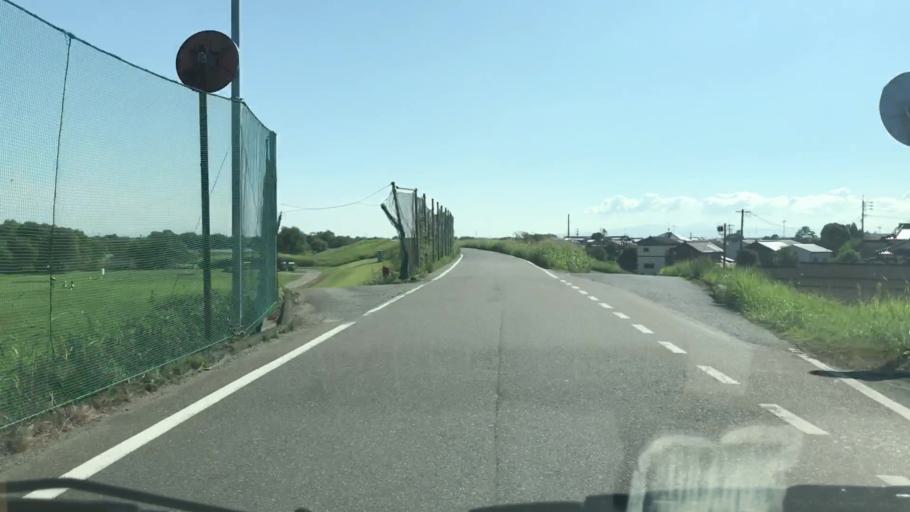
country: JP
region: Fukuoka
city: Kurume
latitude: 33.2819
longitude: 130.4488
